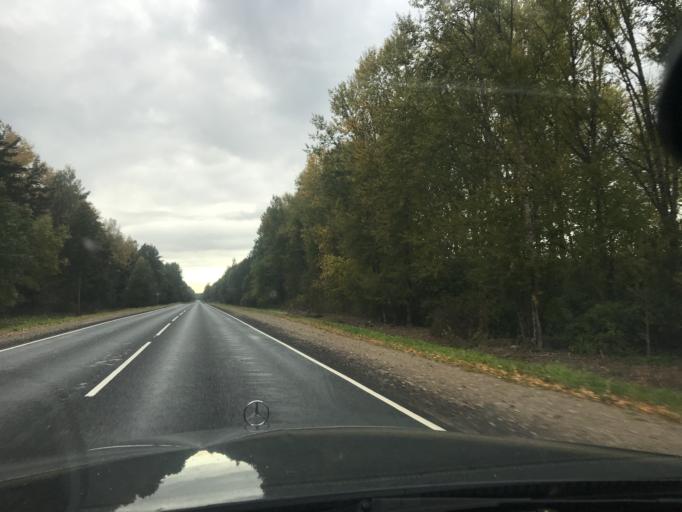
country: RU
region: Pskov
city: Izborsk
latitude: 57.7012
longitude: 27.7305
